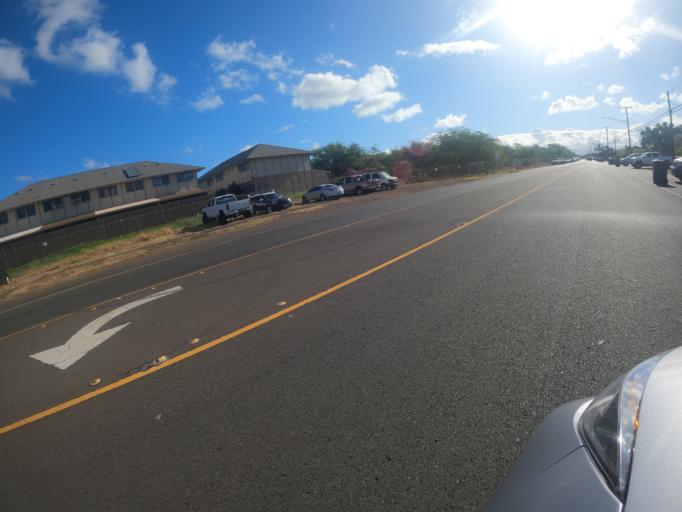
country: US
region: Hawaii
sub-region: Honolulu County
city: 'Ewa Beach
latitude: 21.3132
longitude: -158.0036
